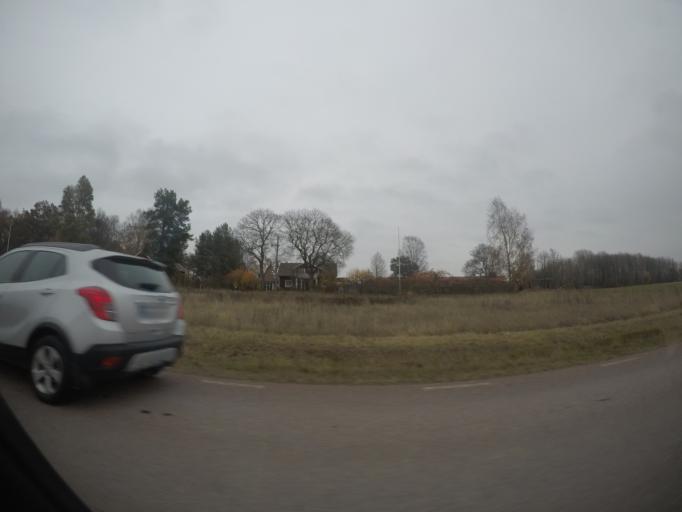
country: SE
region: Vaestmanland
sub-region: Kopings Kommun
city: Koping
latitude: 59.5765
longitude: 16.0835
